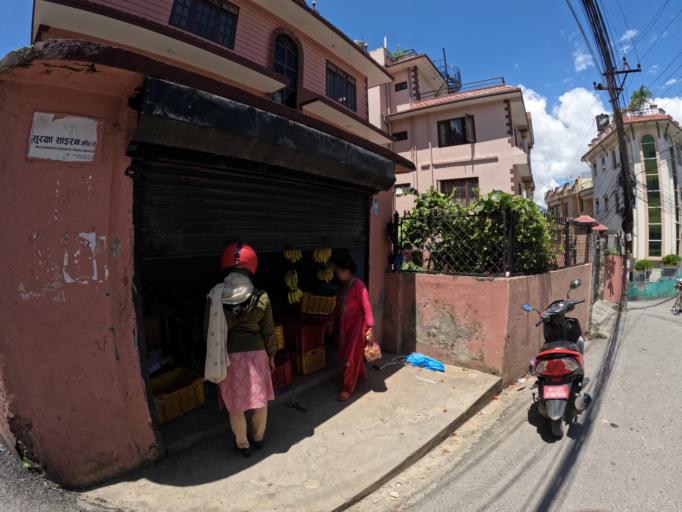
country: NP
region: Central Region
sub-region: Bagmati Zone
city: Kathmandu
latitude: 27.7481
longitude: 85.3275
